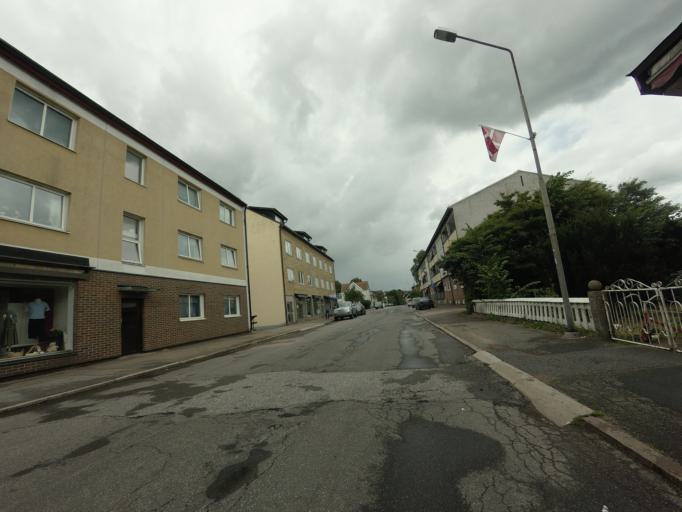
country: SE
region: Skane
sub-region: Osby Kommun
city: Osby
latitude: 56.3824
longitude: 13.9973
